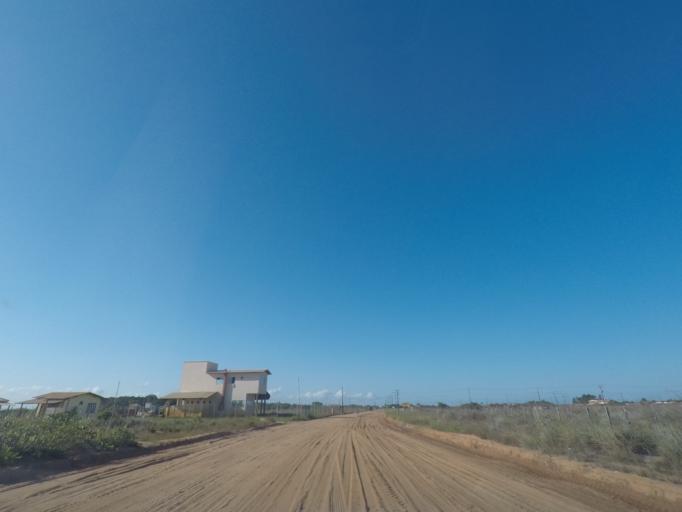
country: BR
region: Bahia
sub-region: Camamu
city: Camamu
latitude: -13.9374
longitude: -38.9466
